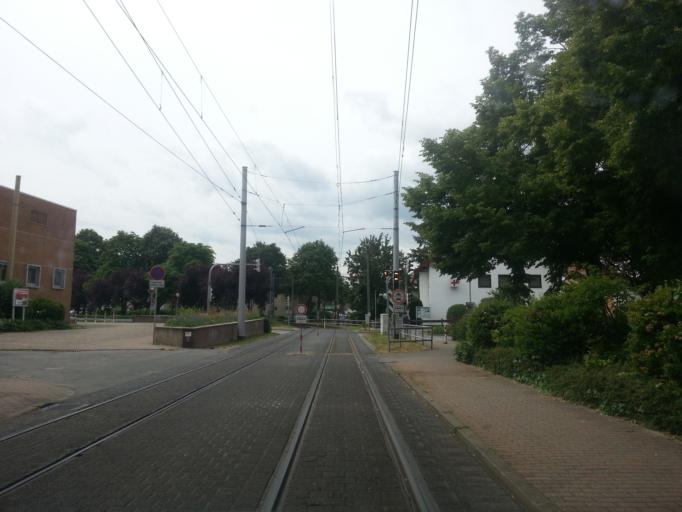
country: DE
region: Hesse
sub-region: Regierungsbezirk Darmstadt
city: Seeheim-Jugenheim
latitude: 49.7664
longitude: 8.6456
